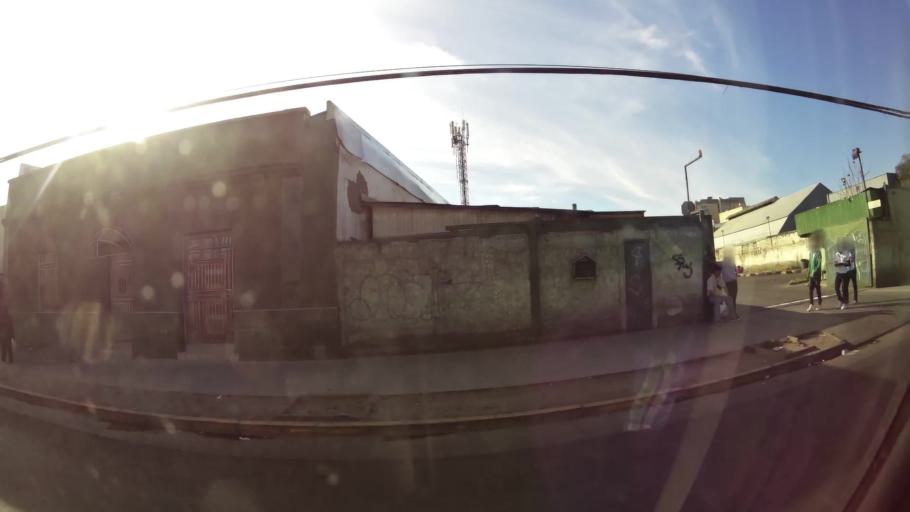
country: CL
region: Santiago Metropolitan
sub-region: Provincia de Santiago
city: Santiago
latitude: -33.4553
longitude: -70.6835
